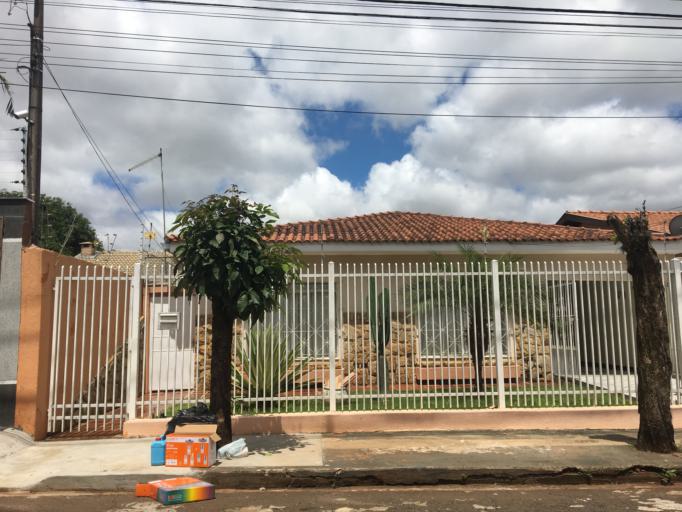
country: BR
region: Parana
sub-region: Londrina
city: Londrina
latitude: -23.2952
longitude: -51.1643
